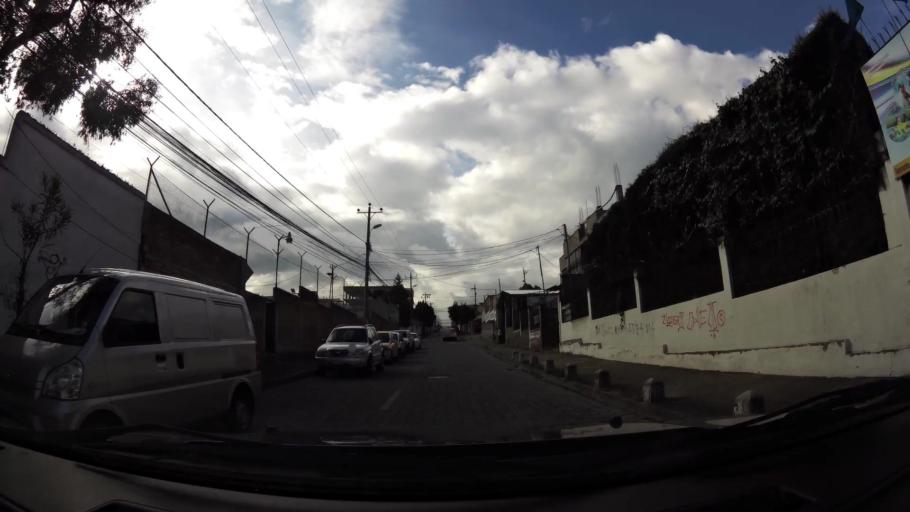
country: EC
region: Pichincha
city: Quito
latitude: -0.1347
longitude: -78.4716
